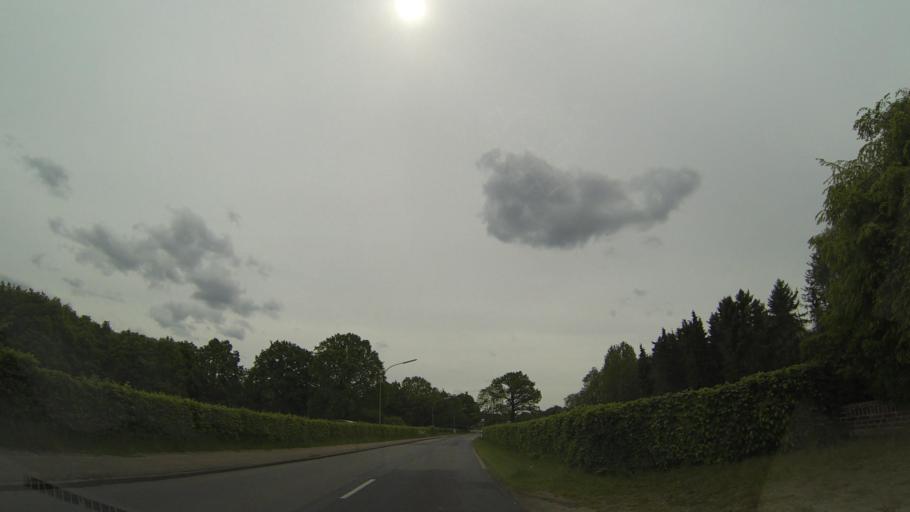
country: DE
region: Schleswig-Holstein
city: Ellerbek
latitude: 53.6408
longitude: 9.8711
